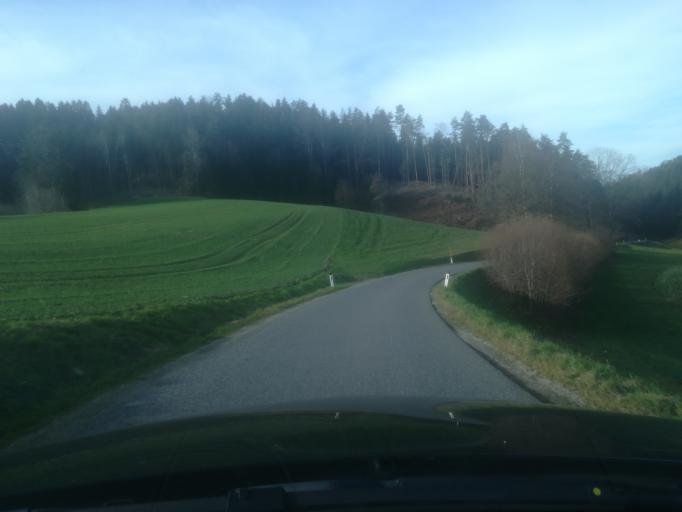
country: AT
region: Upper Austria
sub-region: Politischer Bezirk Perg
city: Perg
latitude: 48.3329
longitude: 14.6490
